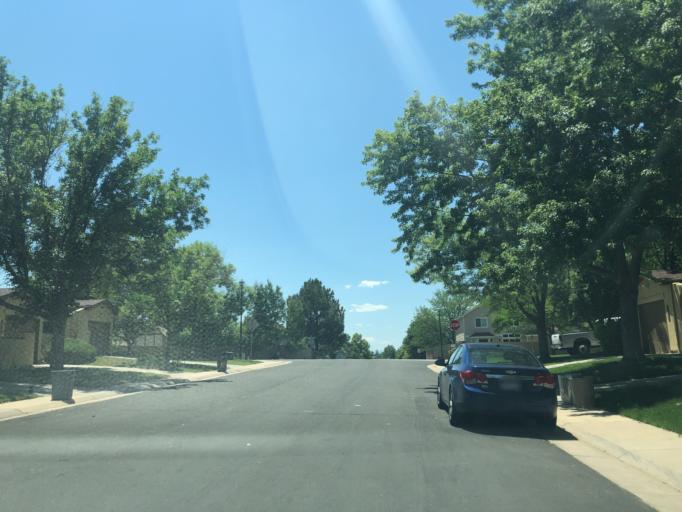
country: US
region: Colorado
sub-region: Arapahoe County
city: Dove Valley
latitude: 39.6279
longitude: -104.7724
